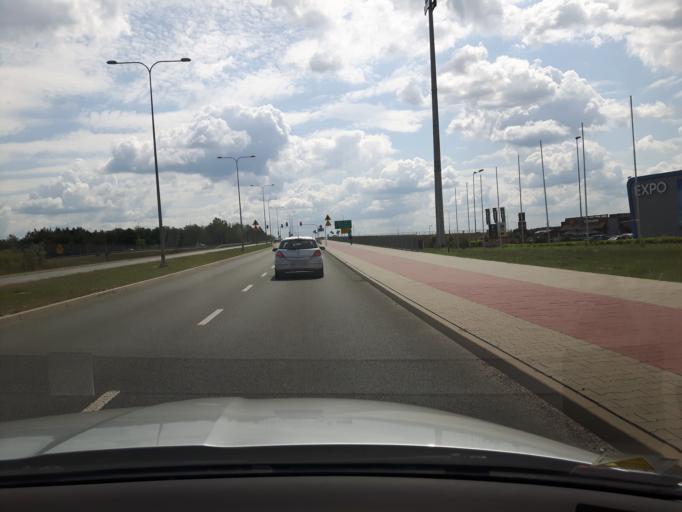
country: PL
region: Masovian Voivodeship
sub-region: Powiat pruszkowski
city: Nadarzyn
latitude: 52.1089
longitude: 20.8348
